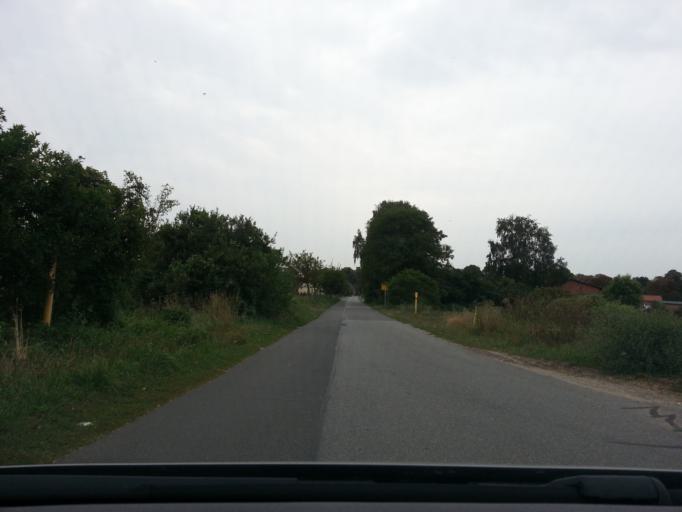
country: DE
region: Mecklenburg-Vorpommern
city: Ferdinandshof
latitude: 53.6479
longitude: 13.9200
